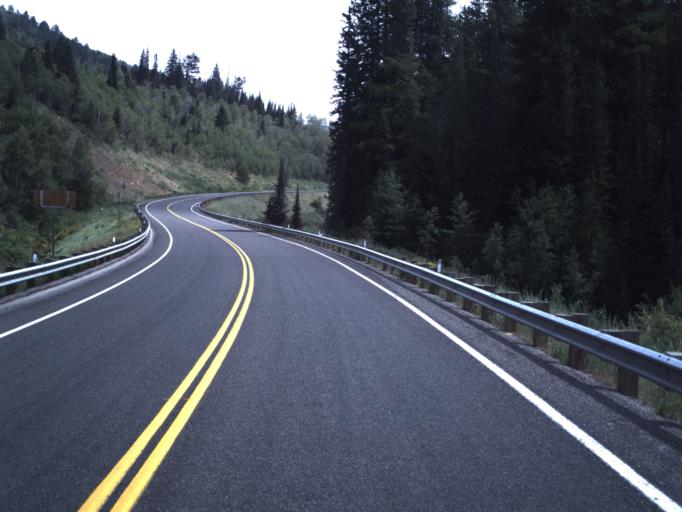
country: US
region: Utah
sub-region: Summit County
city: Francis
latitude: 40.5157
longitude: -111.0718
